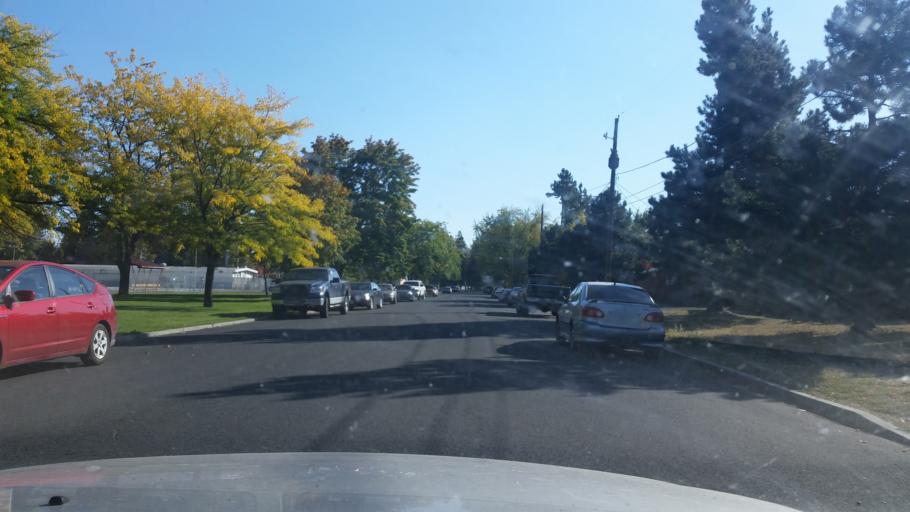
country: US
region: Washington
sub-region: Spokane County
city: Cheney
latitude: 47.4951
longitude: -117.5796
